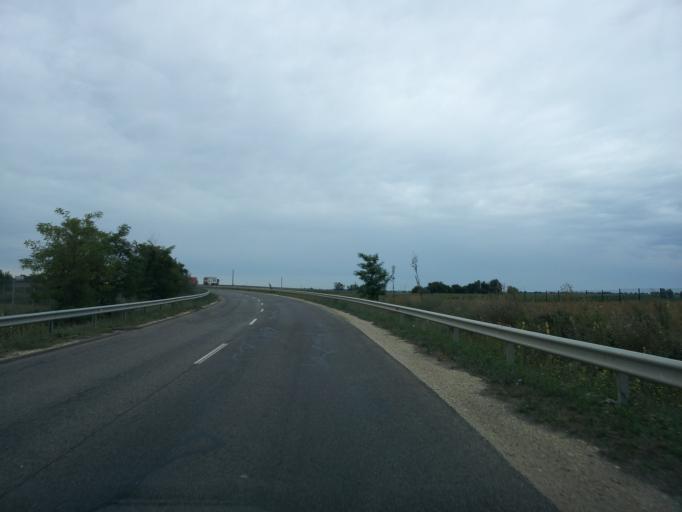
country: HU
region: Pest
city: Tarnok
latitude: 47.3850
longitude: 18.8328
